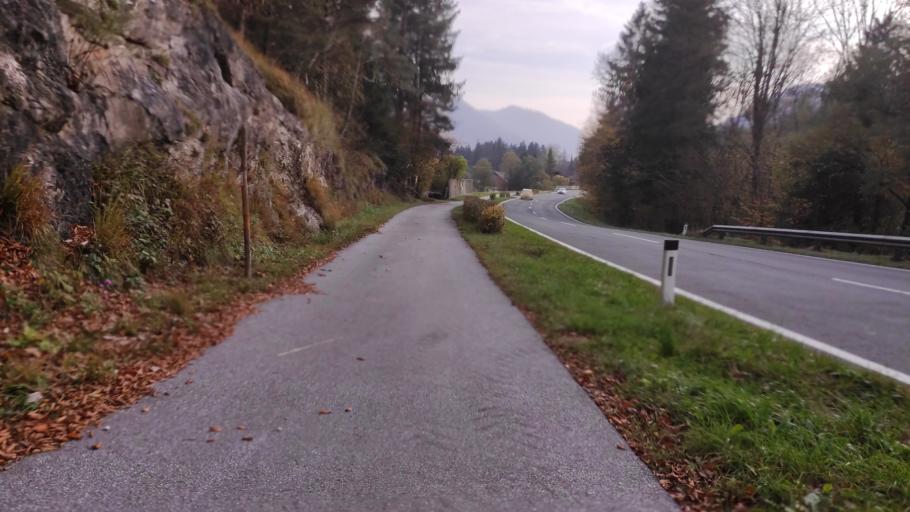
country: AT
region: Salzburg
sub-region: Politischer Bezirk Salzburg-Umgebung
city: Ebenau
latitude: 47.7781
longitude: 13.1814
